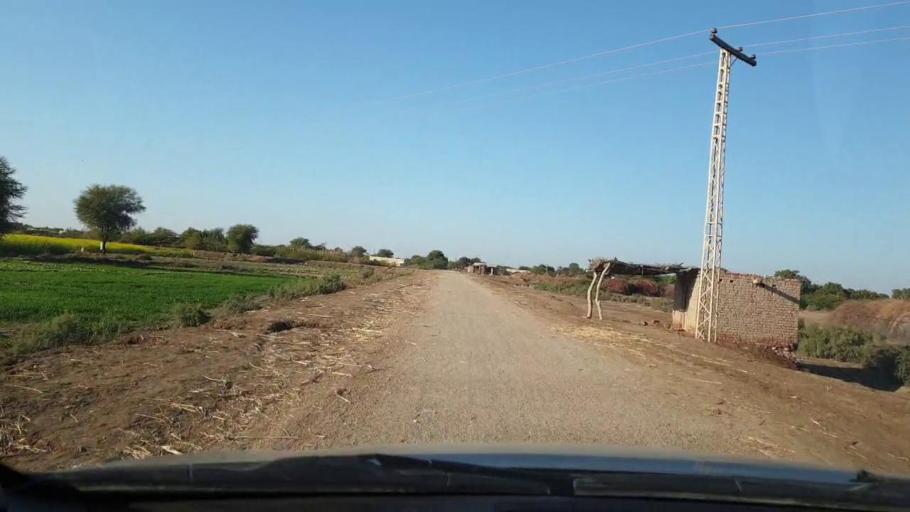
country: PK
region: Sindh
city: Jhol
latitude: 25.8968
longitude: 68.9475
